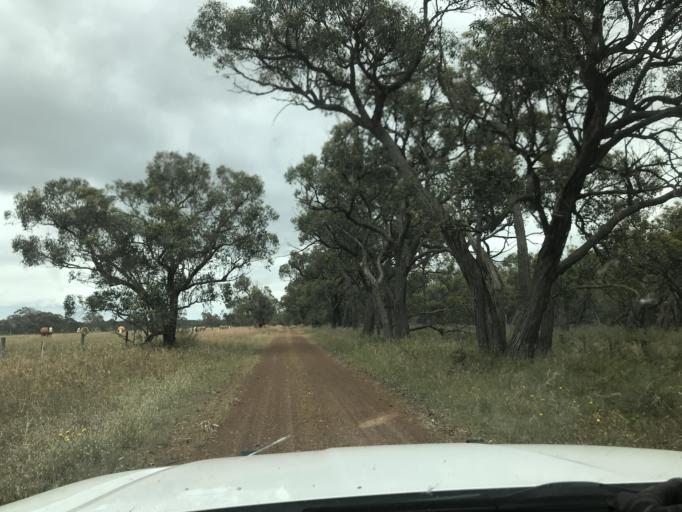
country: AU
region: South Australia
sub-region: Wattle Range
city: Penola
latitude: -37.0983
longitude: 141.2732
